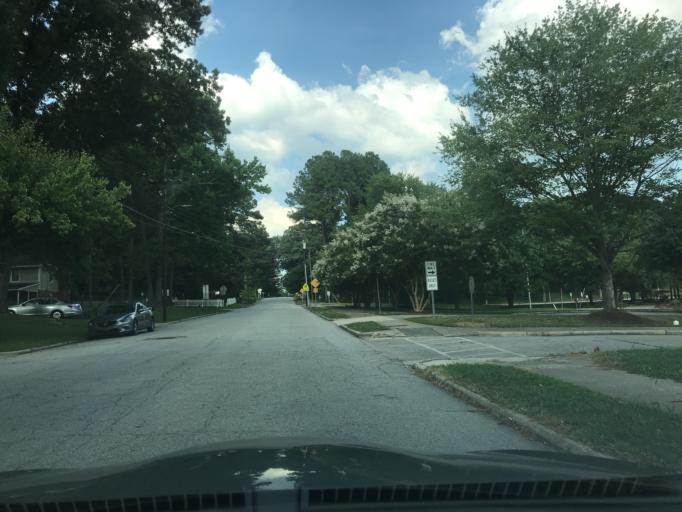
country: US
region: North Carolina
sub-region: Wake County
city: Raleigh
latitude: 35.8310
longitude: -78.5976
